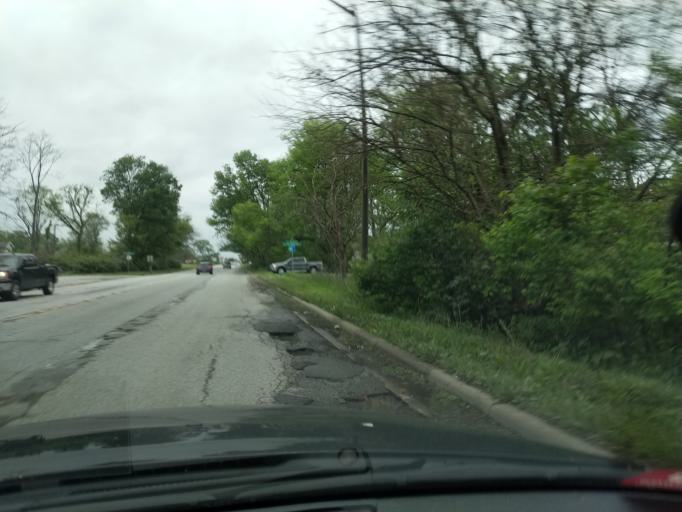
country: US
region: Indiana
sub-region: Marion County
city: Warren Park
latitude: 39.8254
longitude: -86.0916
